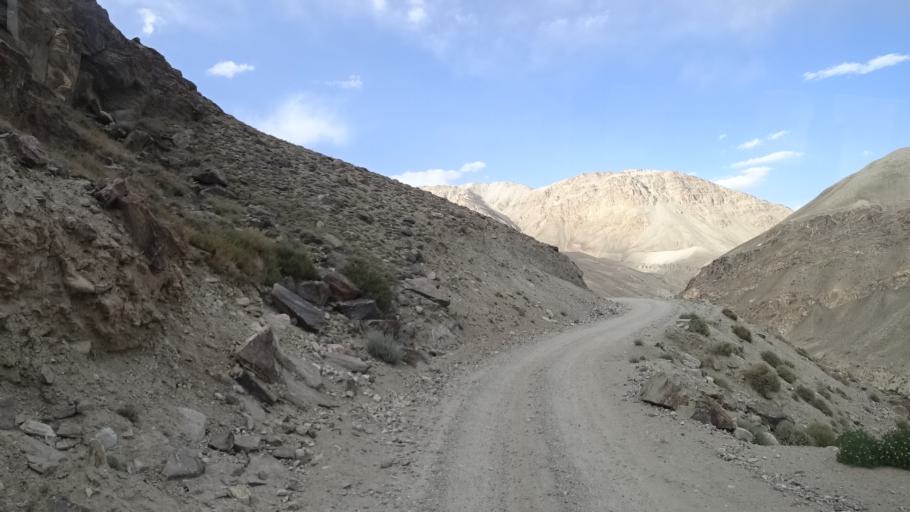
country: AF
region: Badakhshan
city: Khandud
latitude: 37.2280
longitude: 72.8081
